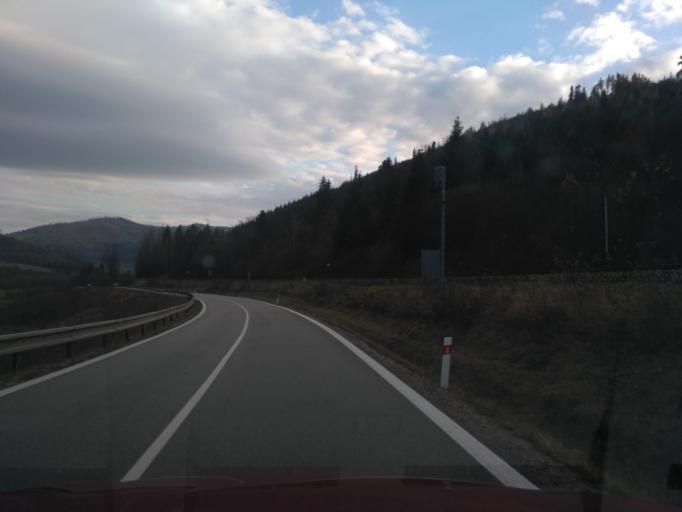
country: SK
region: Kosicky
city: Spisska Nova Ves
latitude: 48.8331
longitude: 20.6465
